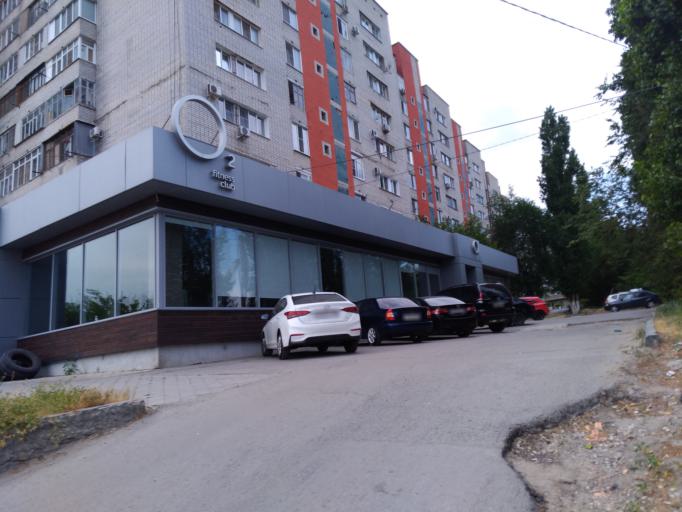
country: RU
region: Volgograd
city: Volgograd
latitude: 48.7073
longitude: 44.4880
